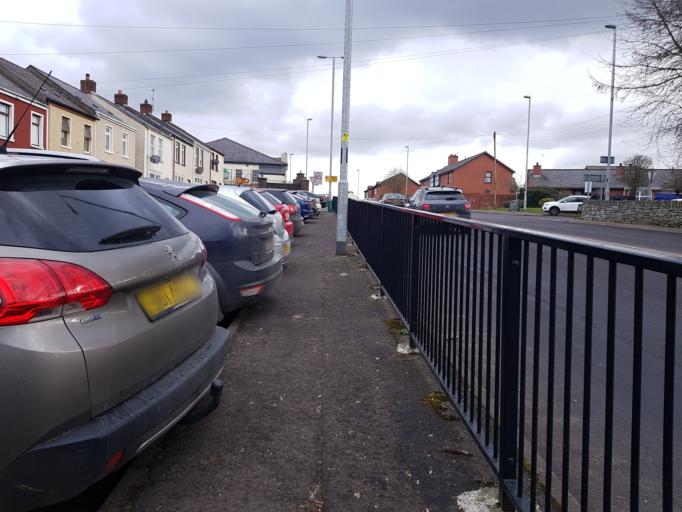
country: GB
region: Northern Ireland
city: Londonderry County Borough
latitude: 54.9925
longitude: -7.3286
